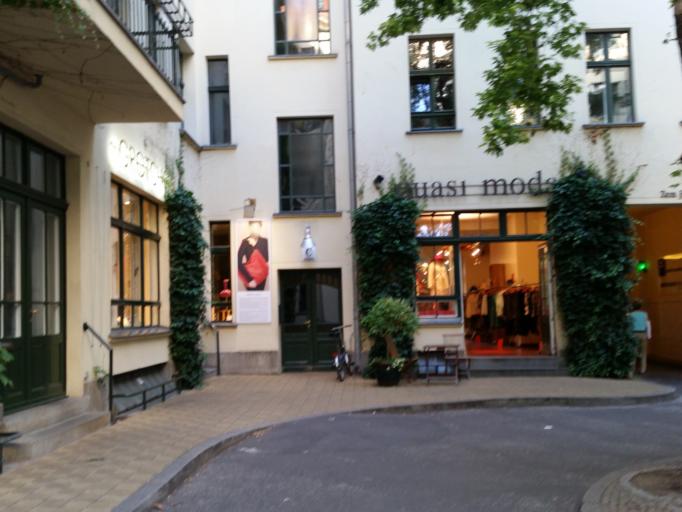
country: DE
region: Berlin
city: Mitte
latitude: 52.5247
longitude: 13.4013
